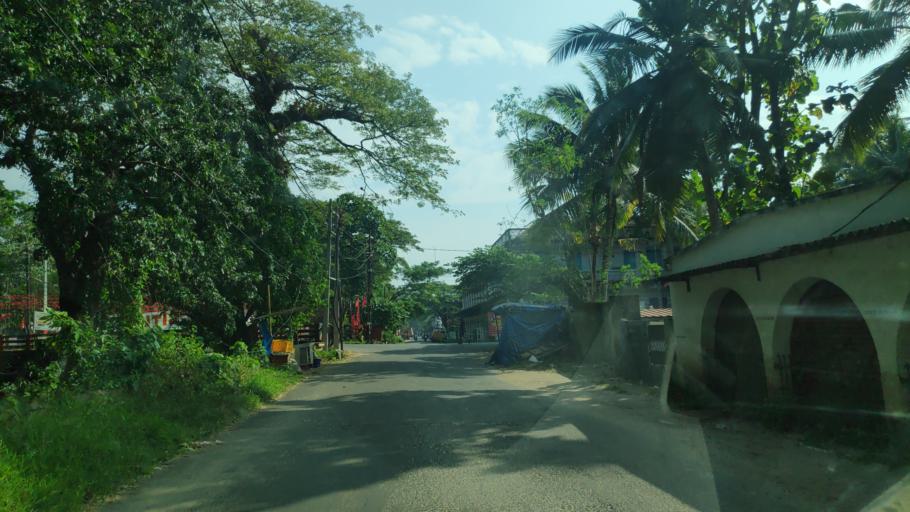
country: IN
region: Kerala
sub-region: Alappuzha
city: Alleppey
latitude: 9.4978
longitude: 76.3216
